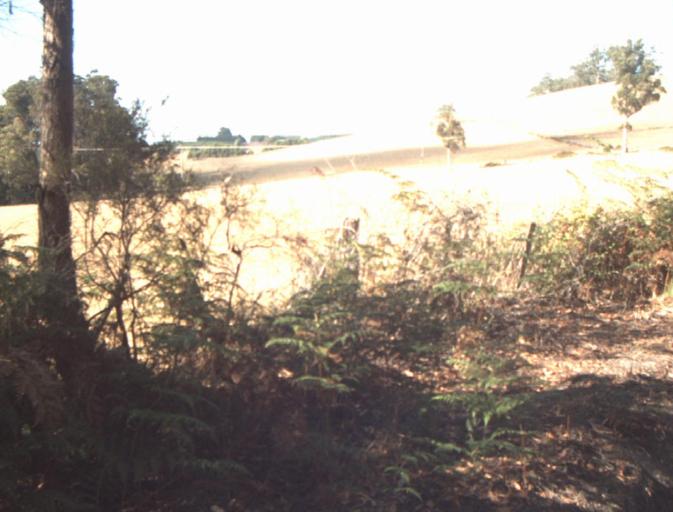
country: AU
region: Tasmania
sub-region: Dorset
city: Bridport
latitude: -41.1523
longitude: 147.2288
